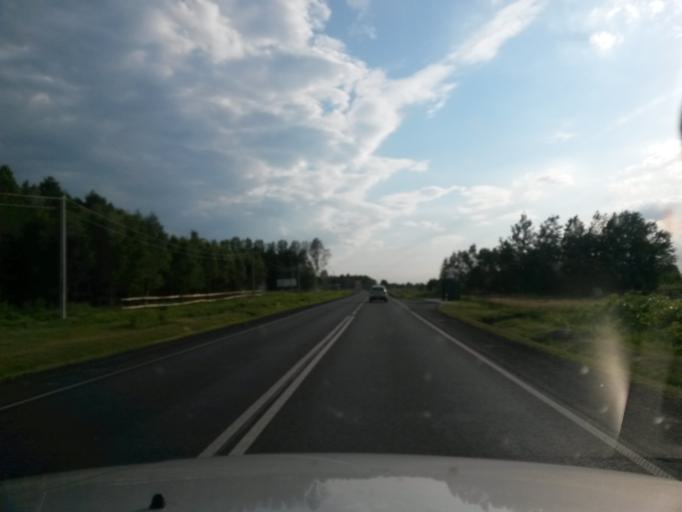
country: PL
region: Lodz Voivodeship
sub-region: Powiat belchatowski
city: Belchatow
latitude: 51.3942
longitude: 19.4129
